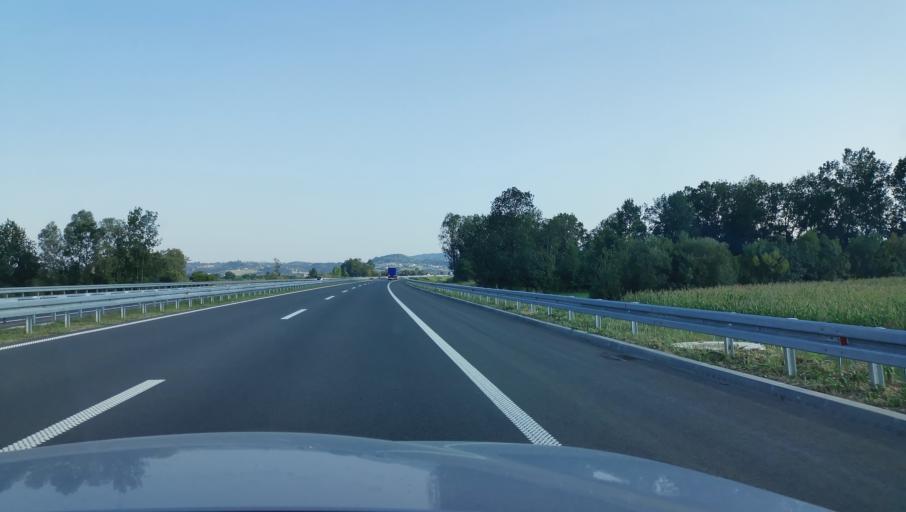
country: RS
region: Central Serbia
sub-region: Kolubarski Okrug
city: Ljig
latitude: 44.2718
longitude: 20.2676
